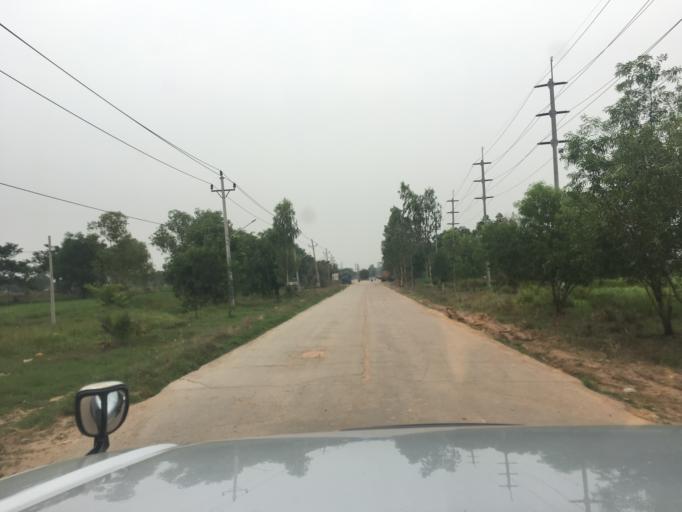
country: MM
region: Yangon
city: Syriam
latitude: 16.9485
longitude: 96.2794
